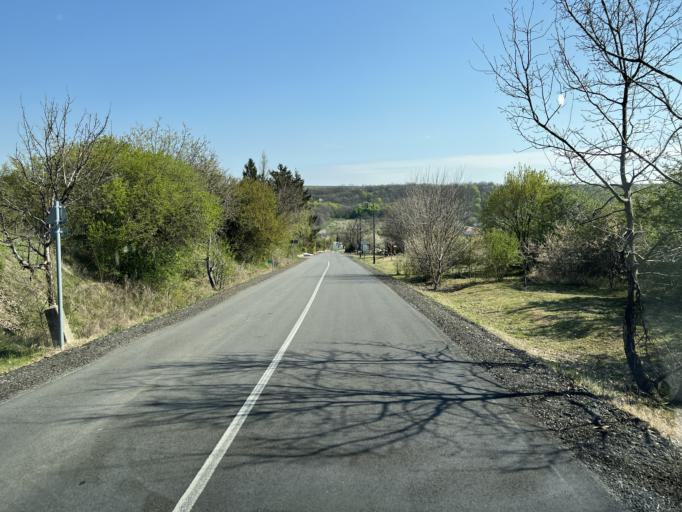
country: HU
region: Pest
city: Orbottyan
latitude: 47.7341
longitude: 19.2874
